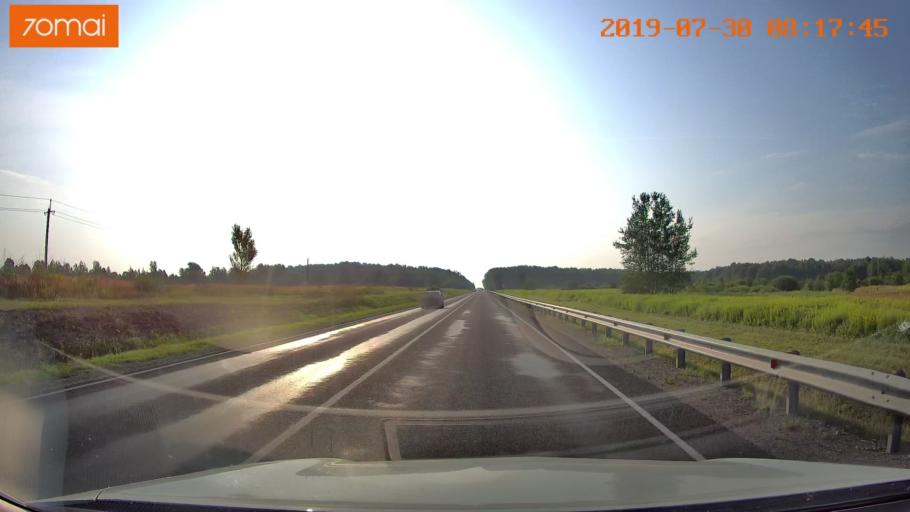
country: RU
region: Kaliningrad
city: Zheleznodorozhnyy
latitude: 54.6351
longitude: 21.4457
